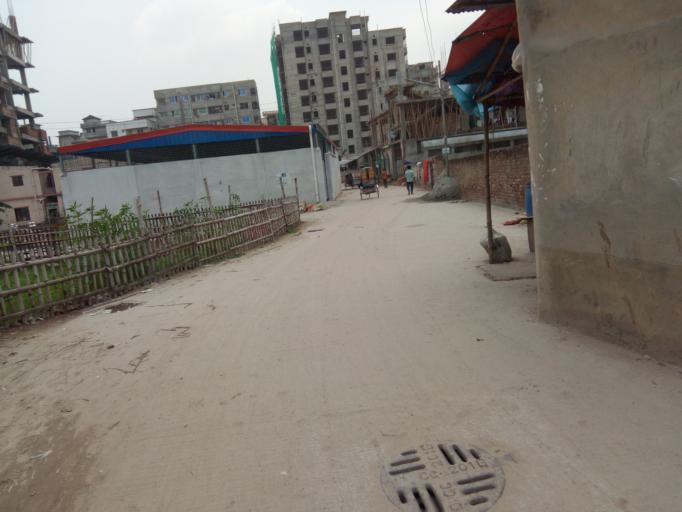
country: BD
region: Dhaka
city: Paltan
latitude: 23.7625
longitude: 90.4256
